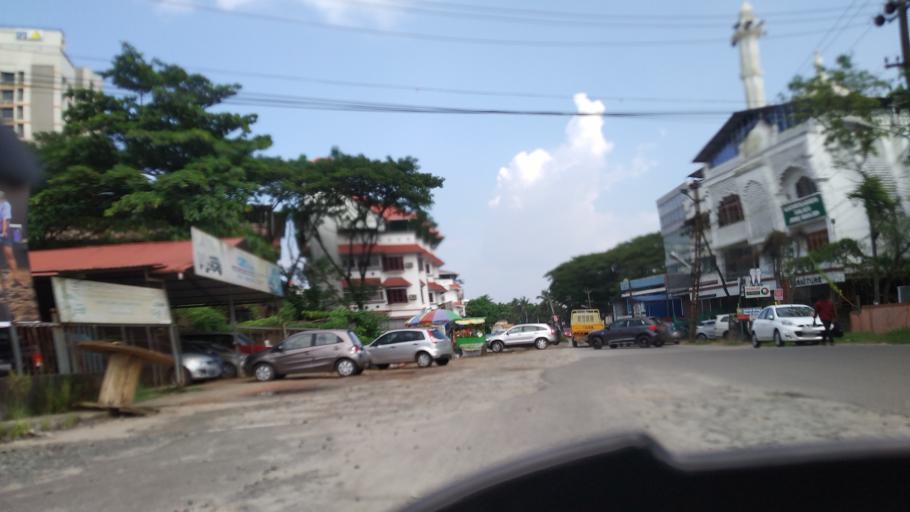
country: IN
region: Kerala
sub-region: Ernakulam
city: Cochin
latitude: 9.9834
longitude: 76.2972
